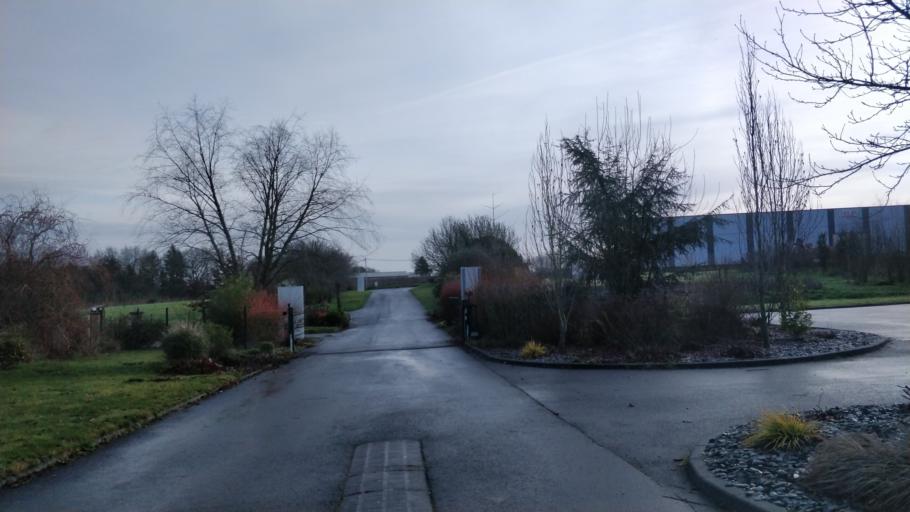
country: FR
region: Brittany
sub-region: Departement d'Ille-et-Vilaine
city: Hede-Bazouges
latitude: 48.2820
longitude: -1.8096
